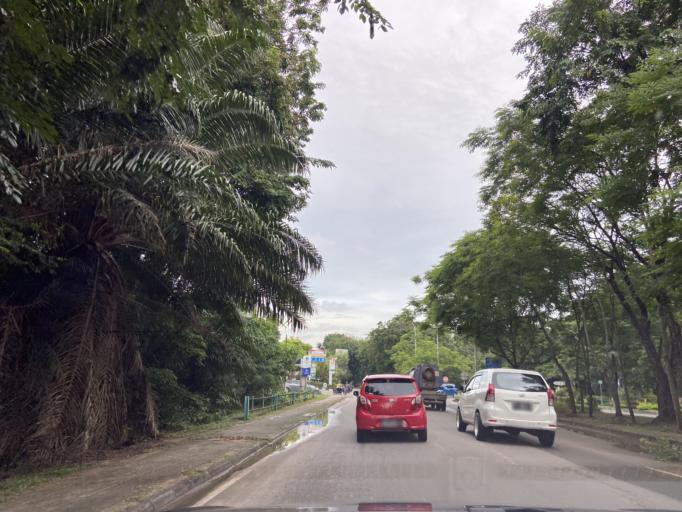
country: SG
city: Singapore
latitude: 1.1106
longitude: 103.9486
